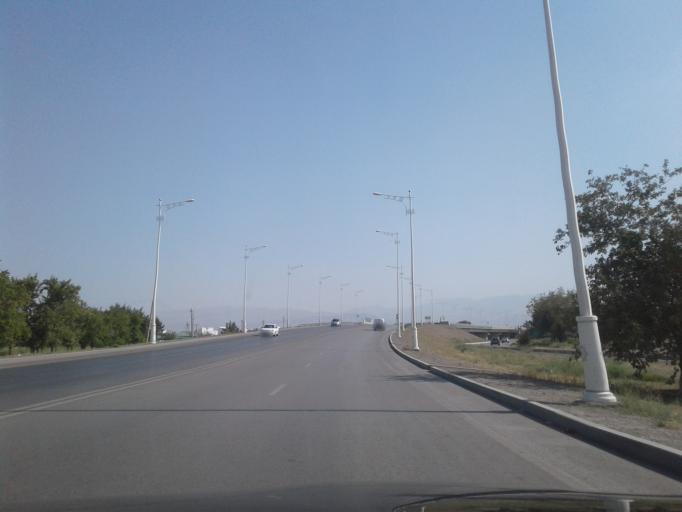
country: TM
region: Ahal
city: Ashgabat
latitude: 37.9671
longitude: 58.4225
